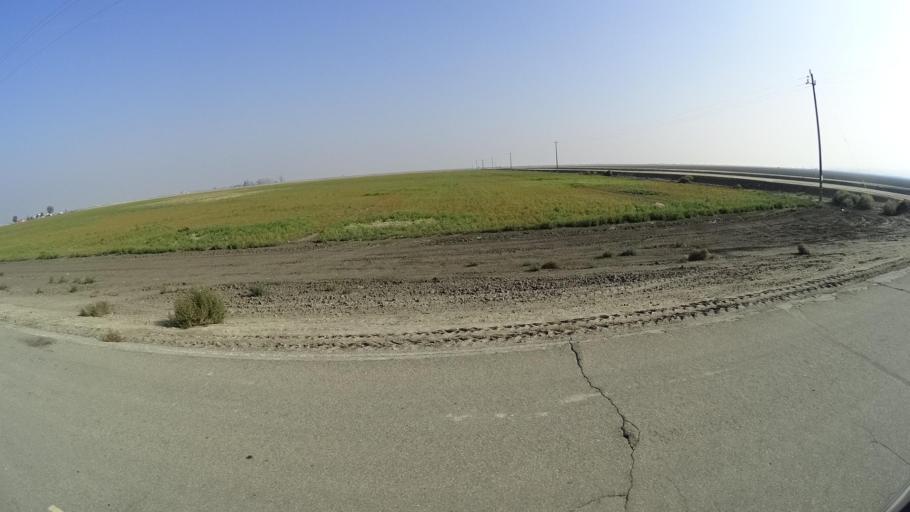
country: US
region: California
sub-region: Kern County
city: Buttonwillow
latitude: 35.3266
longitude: -119.3768
